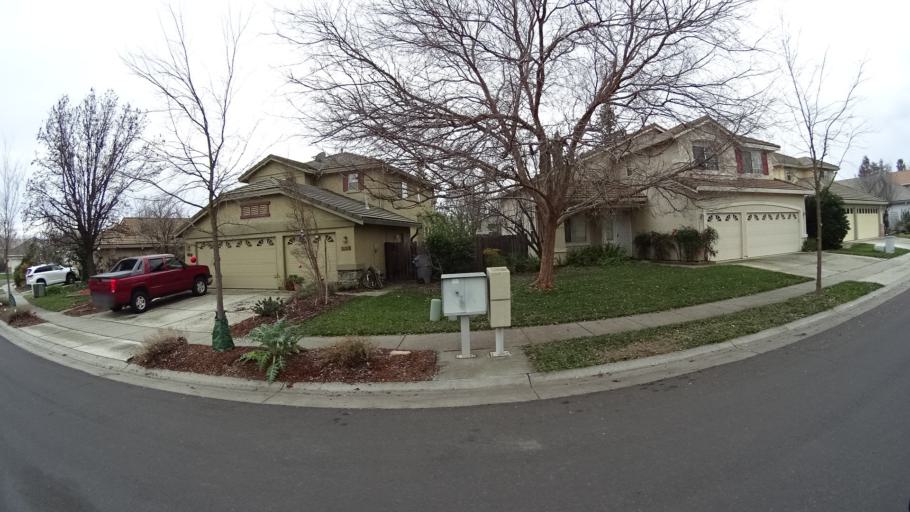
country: US
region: California
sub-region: Yolo County
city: Davis
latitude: 38.5552
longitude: -121.7052
